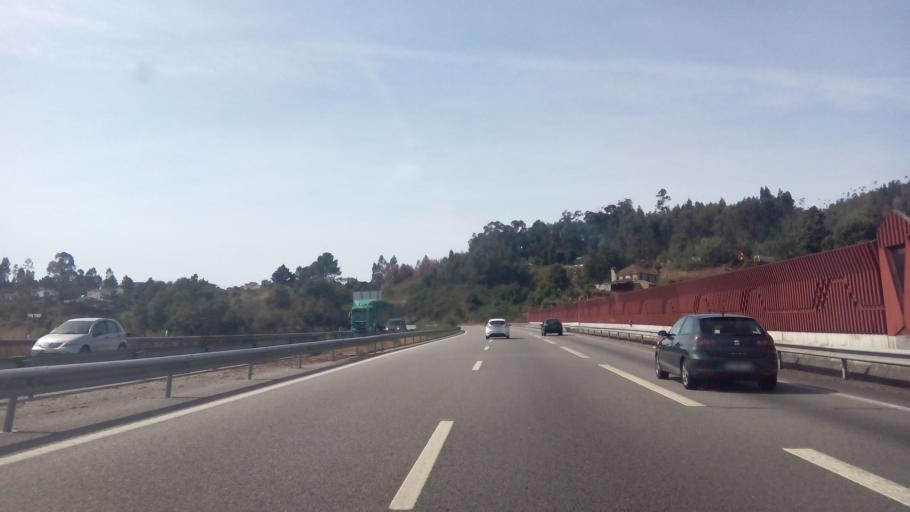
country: PT
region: Porto
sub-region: Lousada
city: Meinedo
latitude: 41.2317
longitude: -8.2172
